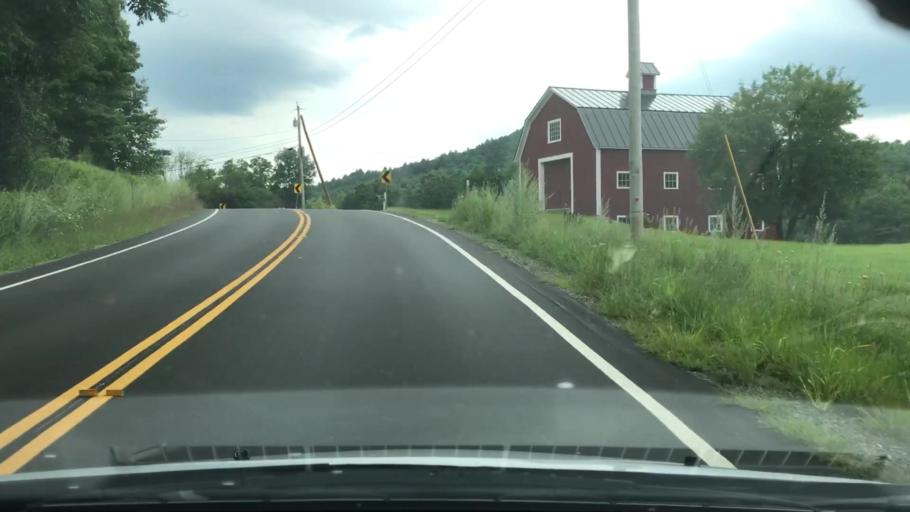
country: US
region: New Hampshire
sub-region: Grafton County
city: Lyme Town Offices
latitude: 43.8443
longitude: -72.1551
